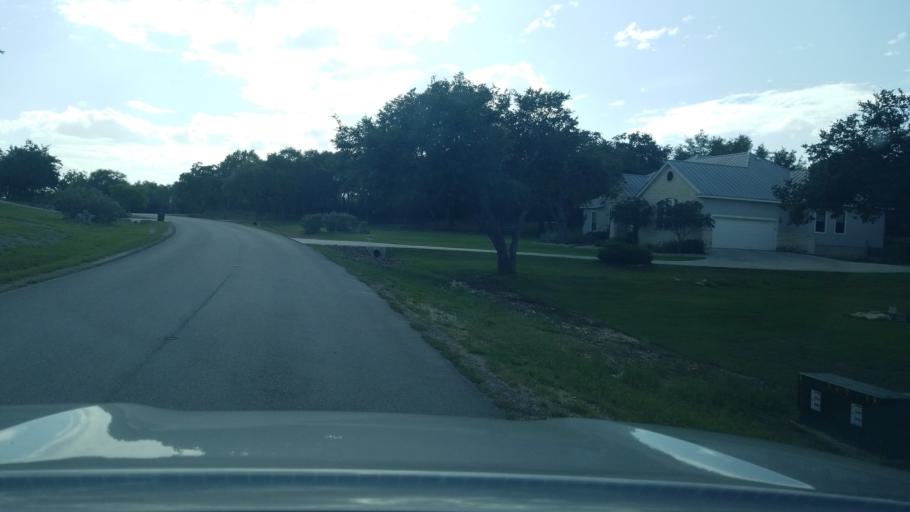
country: US
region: Texas
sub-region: Comal County
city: Bulverde
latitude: 29.8071
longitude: -98.4013
